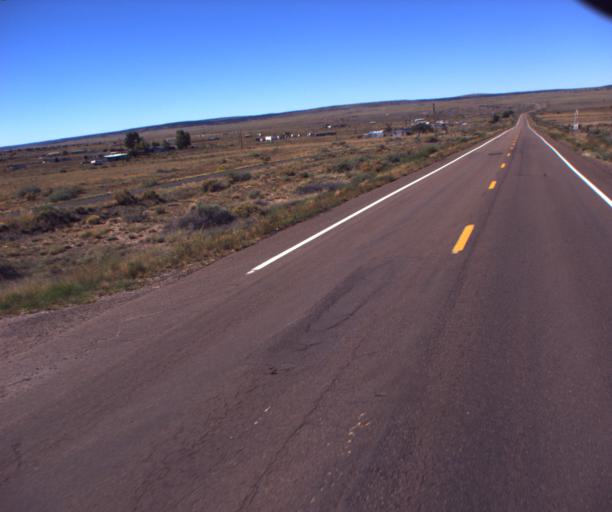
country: US
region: Arizona
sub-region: Apache County
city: Saint Johns
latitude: 34.5069
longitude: -109.4203
